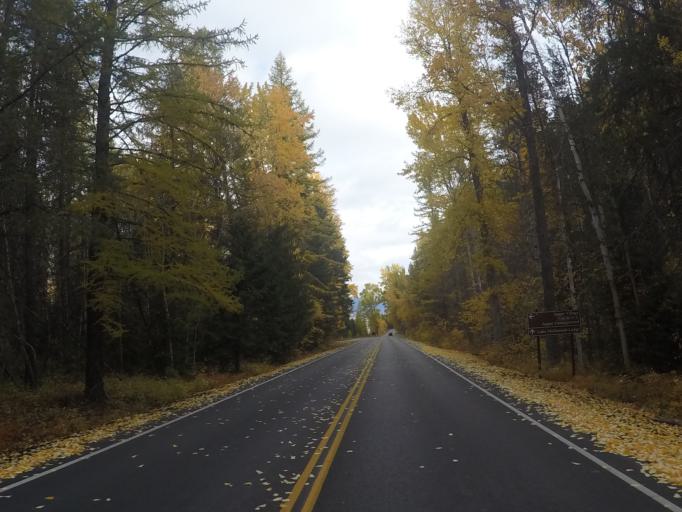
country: US
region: Montana
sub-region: Flathead County
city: Columbia Falls
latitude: 48.5270
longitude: -113.9772
